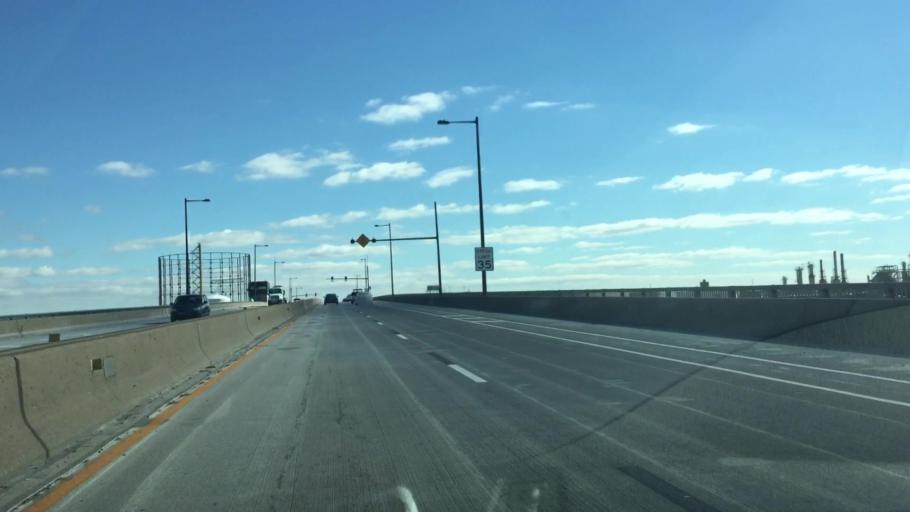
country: US
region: Pennsylvania
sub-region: Delaware County
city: Colwyn
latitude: 39.9192
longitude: -75.2052
